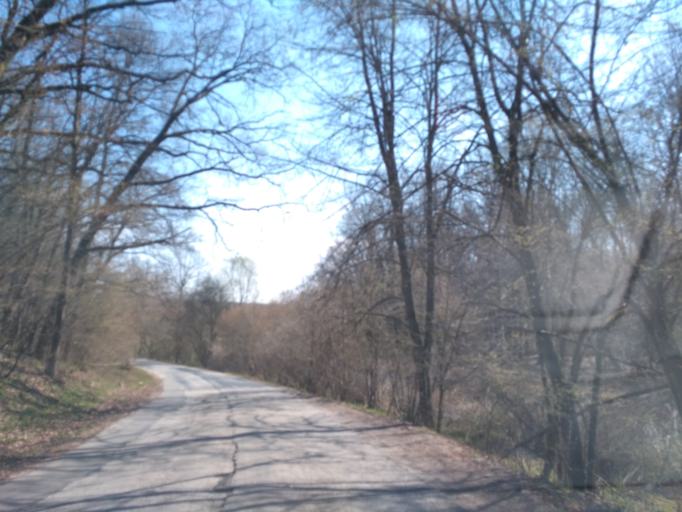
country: SK
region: Kosicky
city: Moldava nad Bodvou
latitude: 48.6463
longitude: 20.9984
